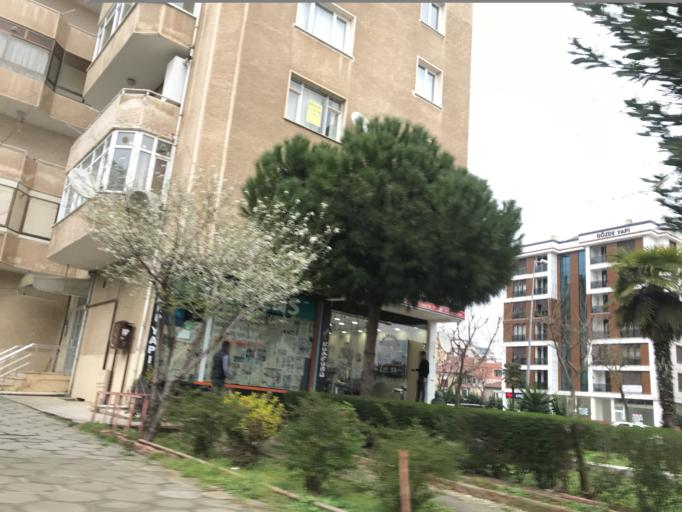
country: TR
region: Istanbul
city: Pendik
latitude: 40.8832
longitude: 29.2305
